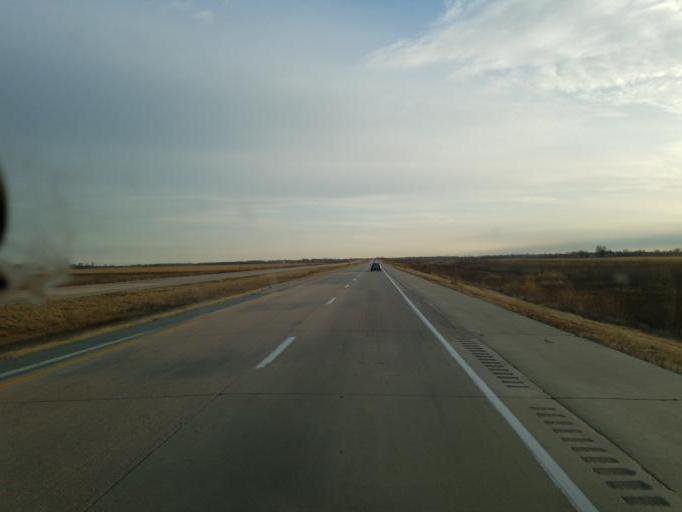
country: US
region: Nebraska
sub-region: Burt County
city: Tekamah
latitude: 41.8746
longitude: -96.1043
